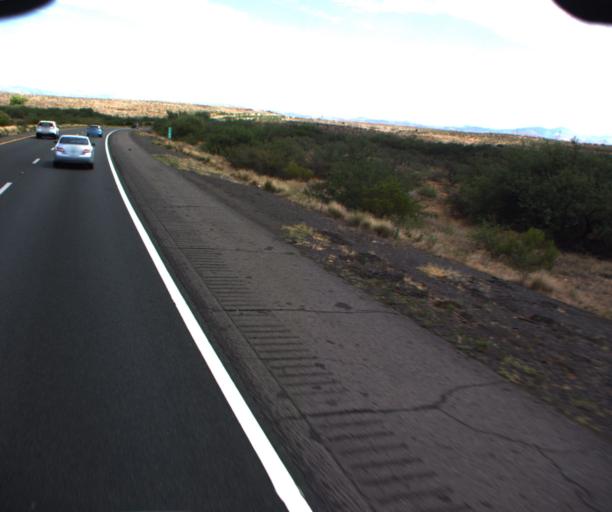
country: US
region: Arizona
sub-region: Yavapai County
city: Spring Valley
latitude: 34.3621
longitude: -112.1166
